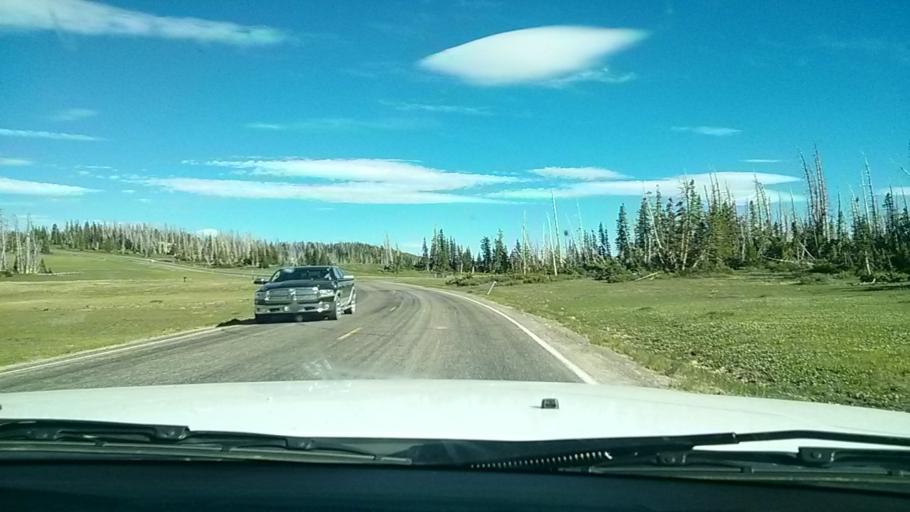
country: US
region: Utah
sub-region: Iron County
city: Parowan
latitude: 37.6586
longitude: -112.8355
